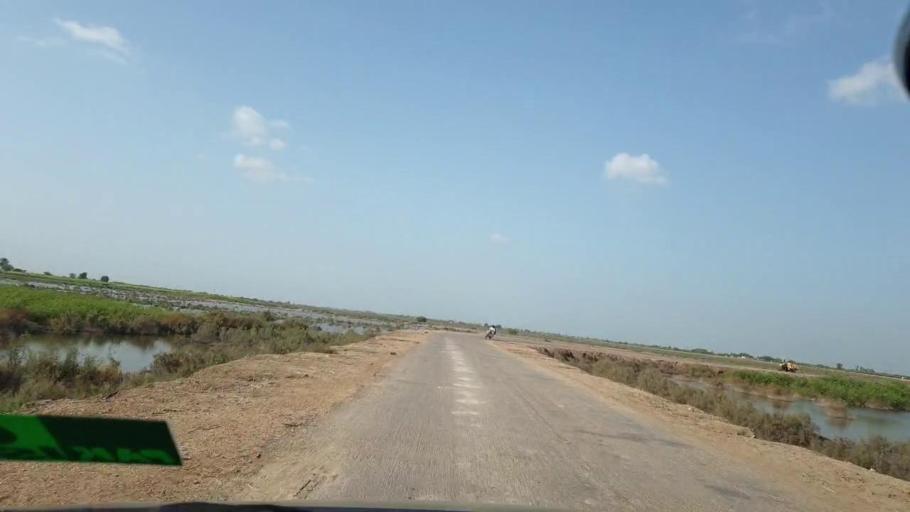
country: PK
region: Sindh
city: Tando Bago
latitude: 24.7246
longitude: 69.1958
